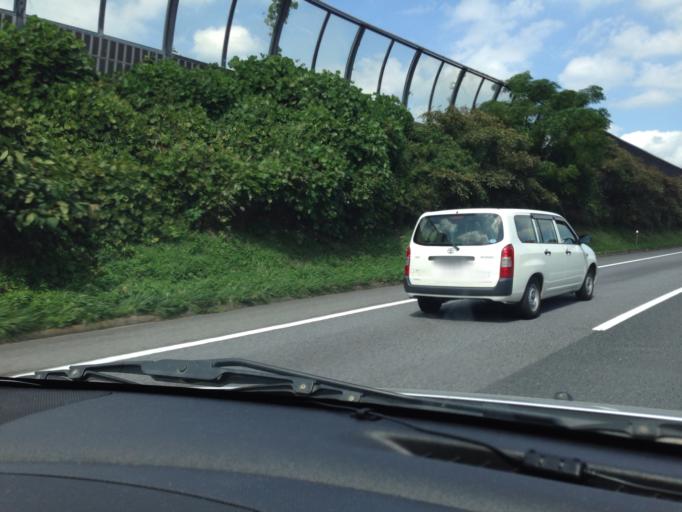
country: JP
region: Ibaraki
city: Naka
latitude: 36.1145
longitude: 140.1812
